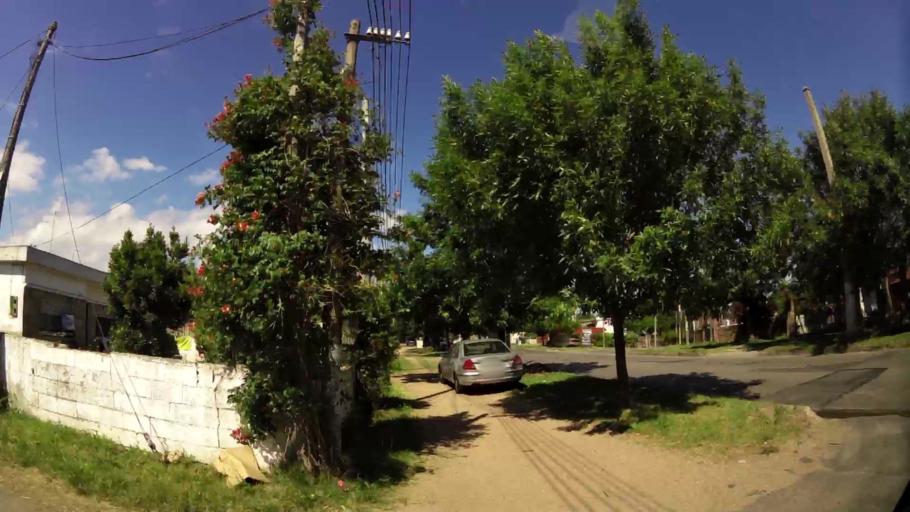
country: UY
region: Canelones
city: La Paz
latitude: -34.8366
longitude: -56.2581
